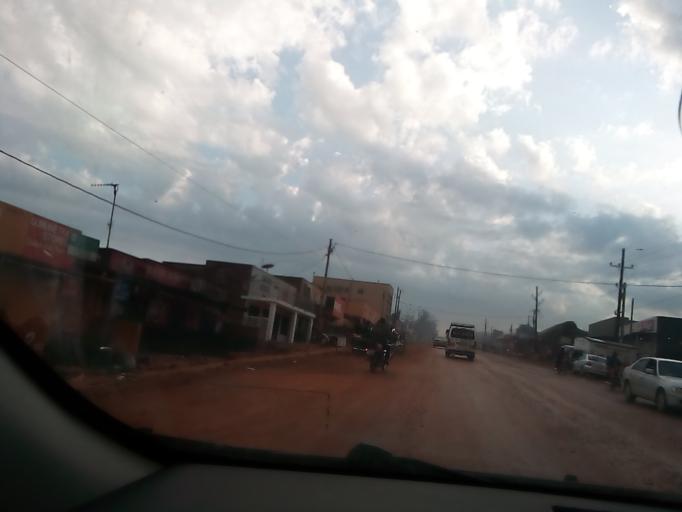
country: UG
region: Central Region
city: Masaka
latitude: -0.3158
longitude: 31.7604
